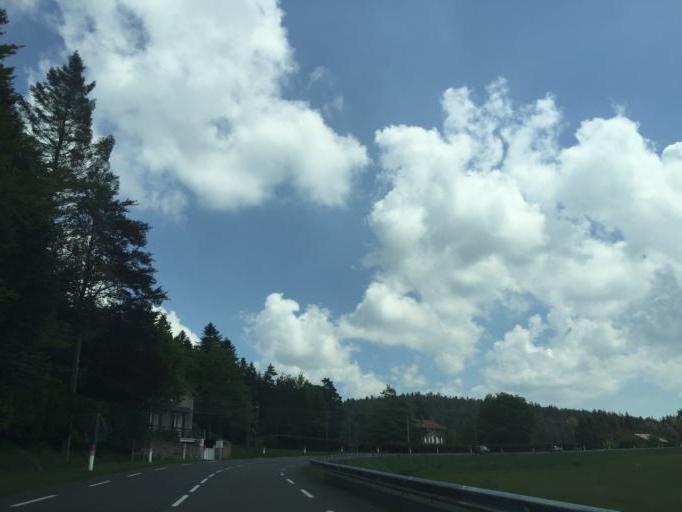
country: FR
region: Rhone-Alpes
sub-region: Departement de la Loire
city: Saint-Genest-Malifaux
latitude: 45.3683
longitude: 4.4503
